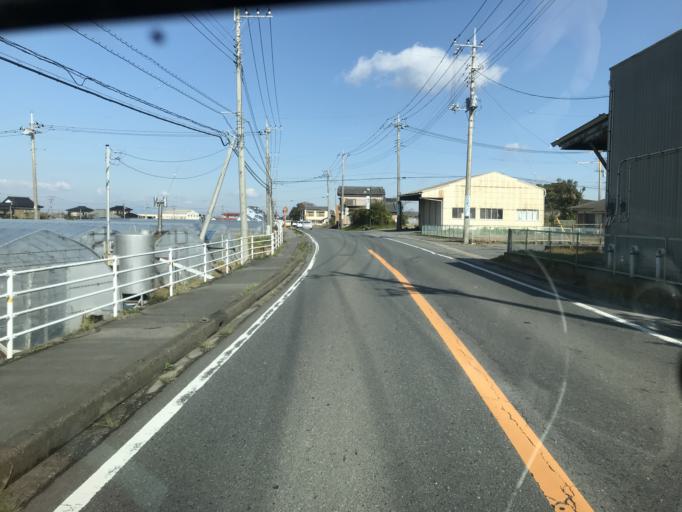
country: JP
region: Ibaraki
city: Itako
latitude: 35.9916
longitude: 140.4761
